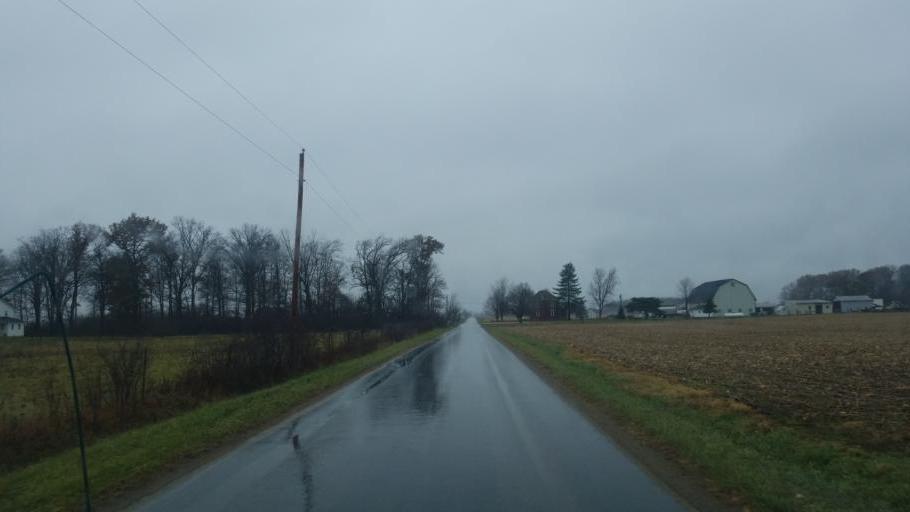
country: US
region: Indiana
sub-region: Adams County
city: Berne
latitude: 40.6333
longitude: -84.8974
